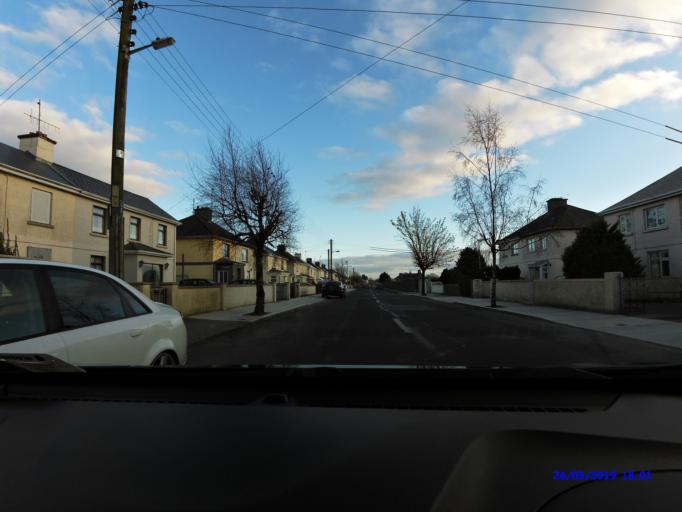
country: IE
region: Connaught
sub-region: County Galway
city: Tuam
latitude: 53.5100
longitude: -8.8447
